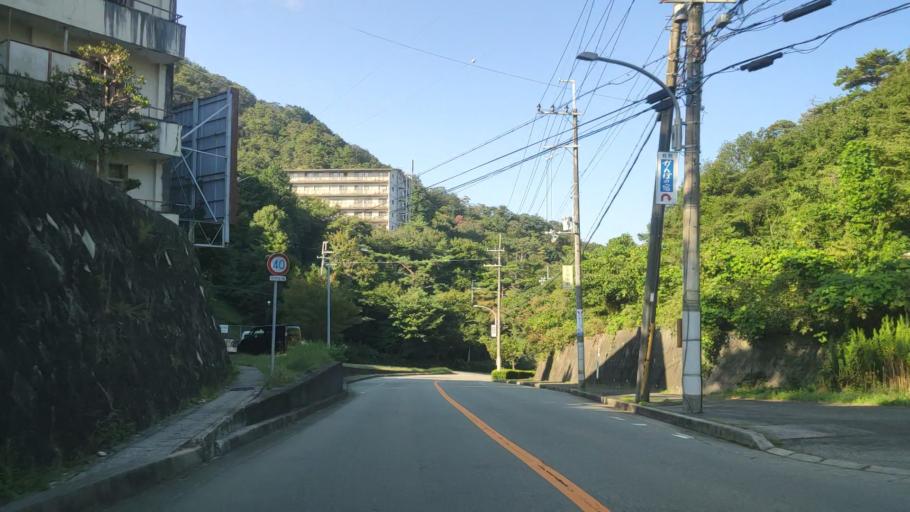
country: JP
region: Hyogo
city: Sandacho
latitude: 34.7986
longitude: 135.2429
